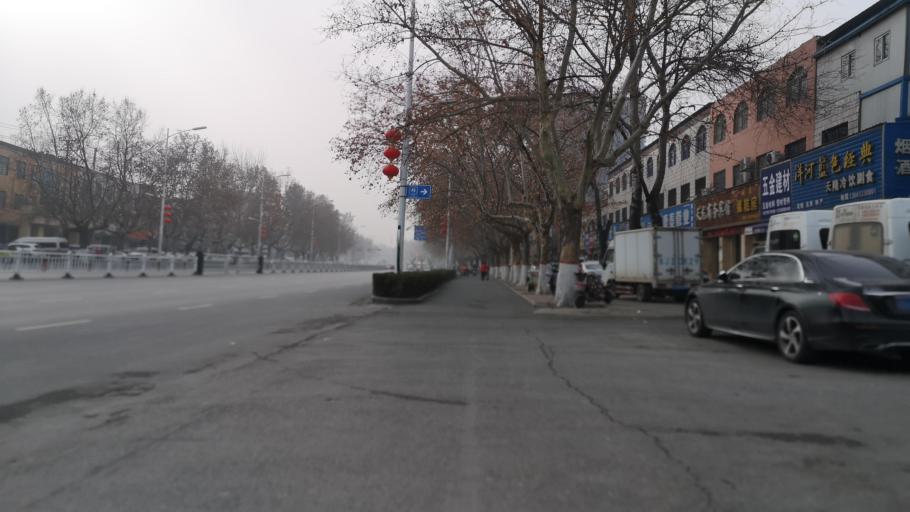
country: CN
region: Henan Sheng
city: Zhongyuanlu
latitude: 35.7744
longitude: 115.0400
